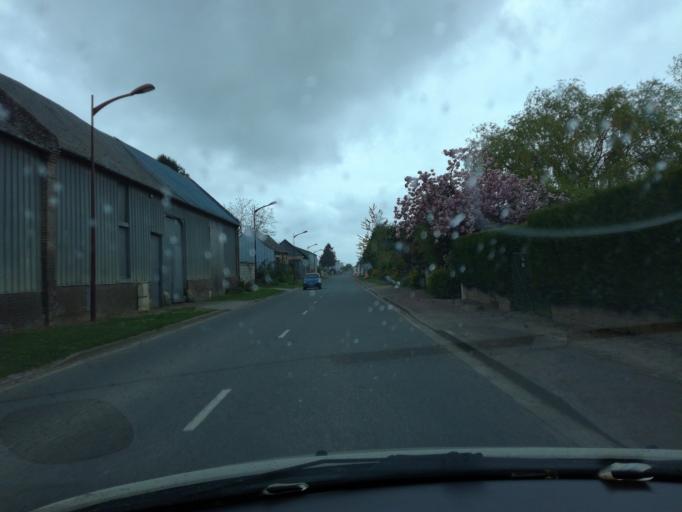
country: FR
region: Picardie
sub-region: Departement de la Somme
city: Hornoy-le-Bourg
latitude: 49.8265
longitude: 1.9404
